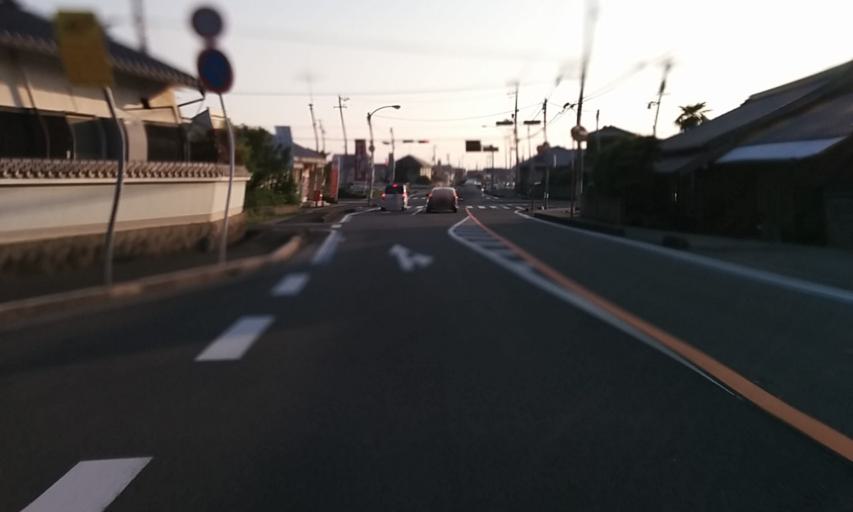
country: JP
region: Ehime
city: Masaki-cho
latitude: 33.7755
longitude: 132.7500
